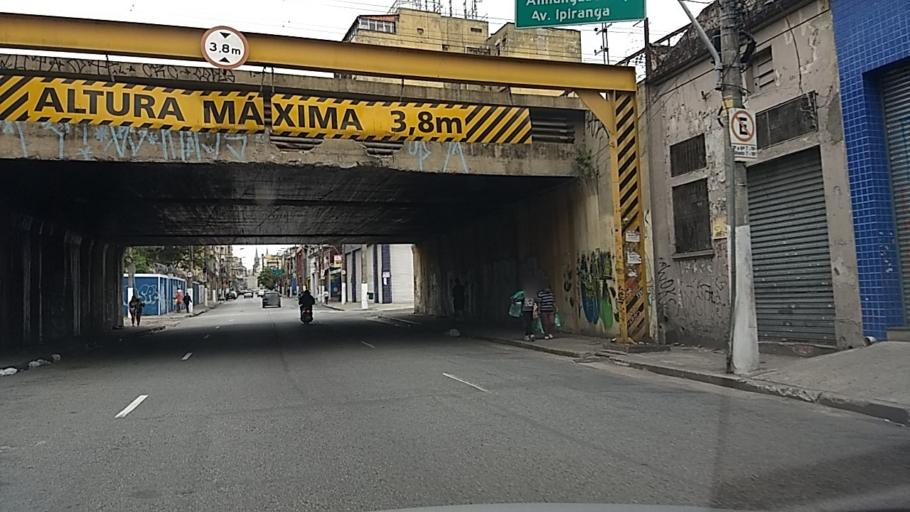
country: BR
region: Sao Paulo
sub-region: Sao Paulo
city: Sao Paulo
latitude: -23.5368
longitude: -46.6280
